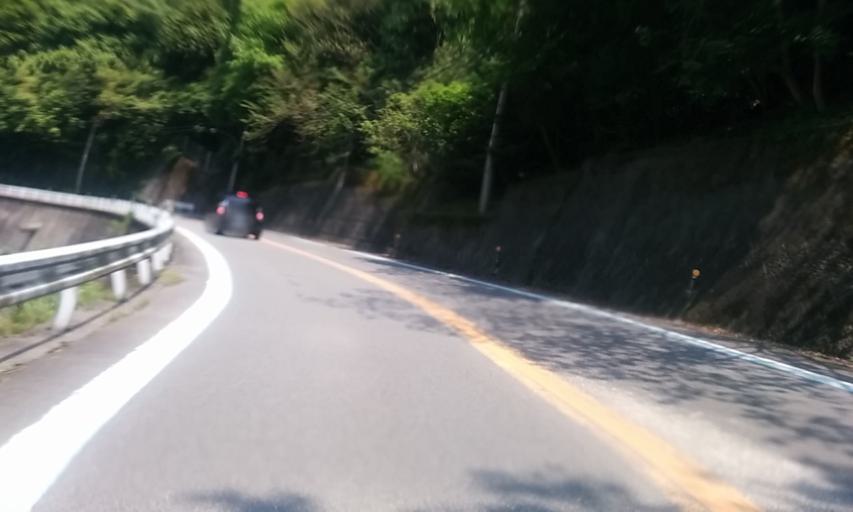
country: JP
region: Ehime
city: Niihama
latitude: 33.9167
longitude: 133.3130
